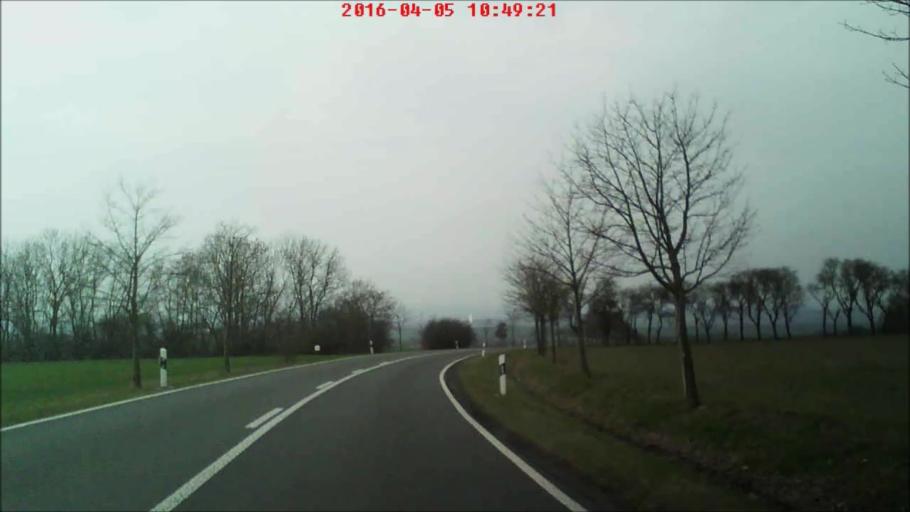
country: DE
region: Thuringia
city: Trochtelborn
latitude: 51.0205
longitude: 10.8159
